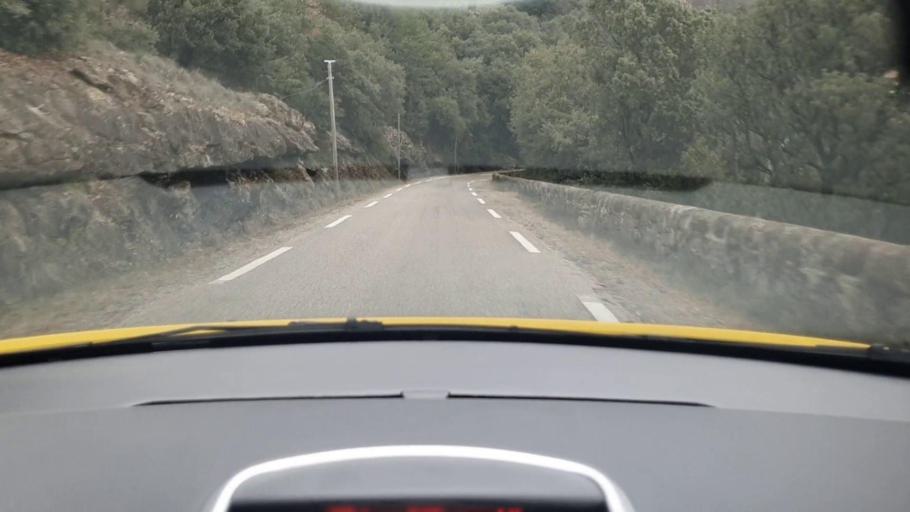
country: FR
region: Languedoc-Roussillon
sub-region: Departement du Gard
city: Besseges
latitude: 44.3455
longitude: 4.0315
